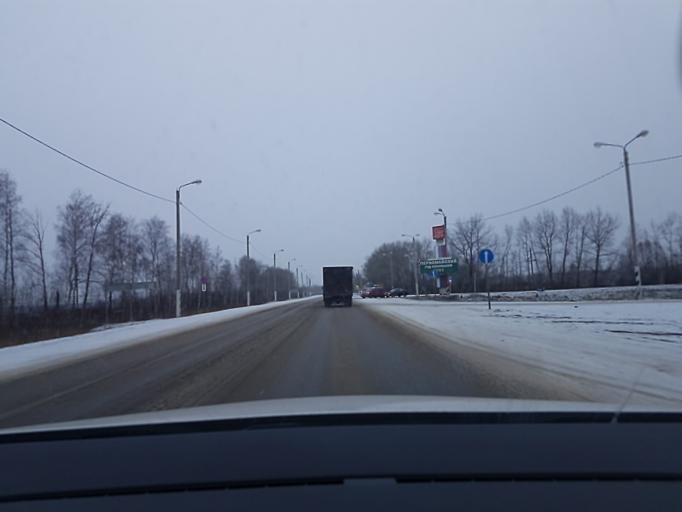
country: RU
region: Tambov
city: Pervomayskiy
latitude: 53.2451
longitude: 40.2545
